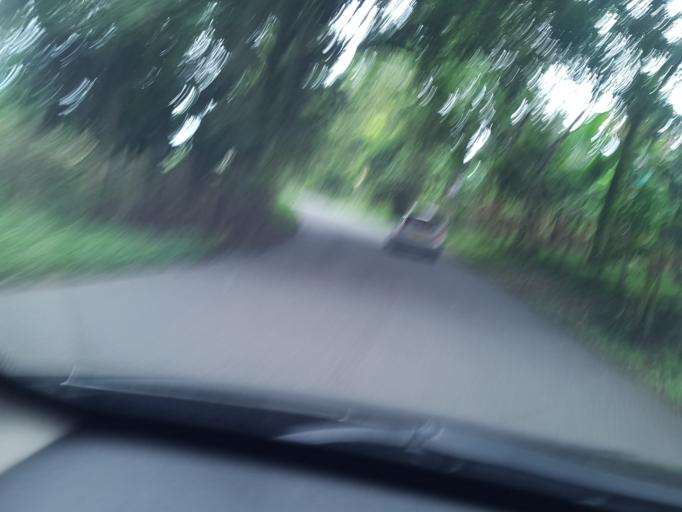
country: CO
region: Quindio
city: La Tebaida
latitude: 4.5044
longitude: -75.7917
